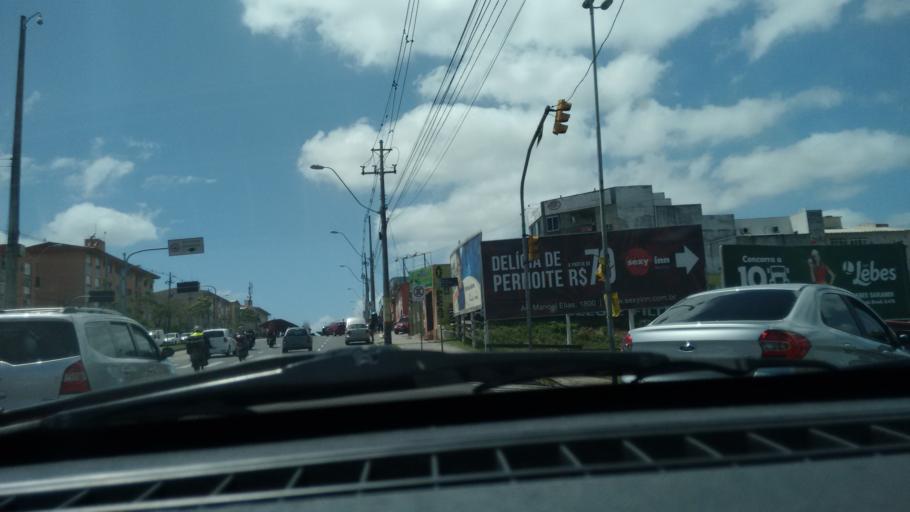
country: BR
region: Rio Grande do Sul
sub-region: Cachoeirinha
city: Cachoeirinha
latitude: -30.0151
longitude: -51.1193
